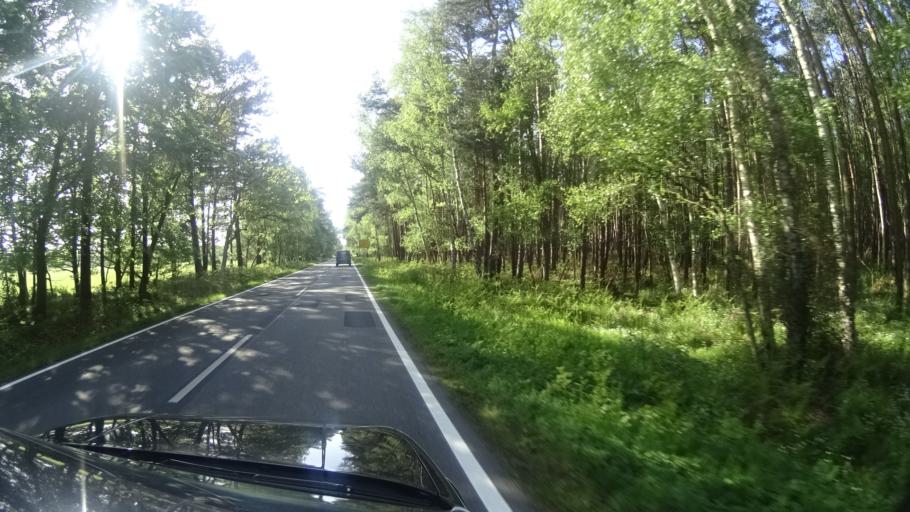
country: DE
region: Mecklenburg-Vorpommern
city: Born
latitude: 54.3974
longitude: 12.4981
